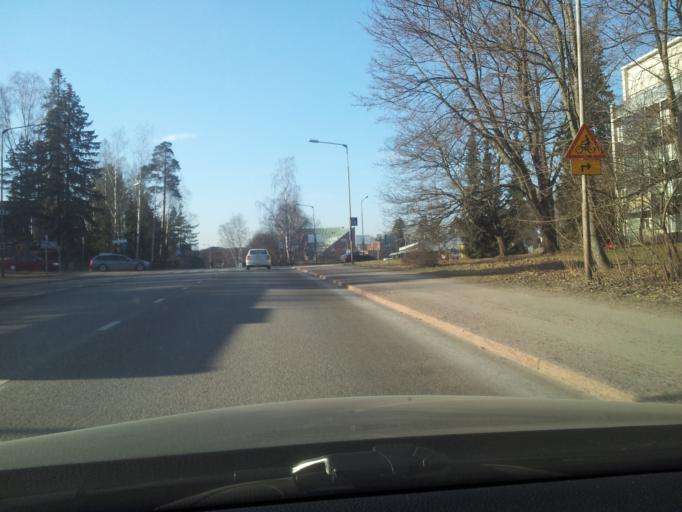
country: FI
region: Uusimaa
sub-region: Helsinki
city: Otaniemi
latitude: 60.1828
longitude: 24.8323
